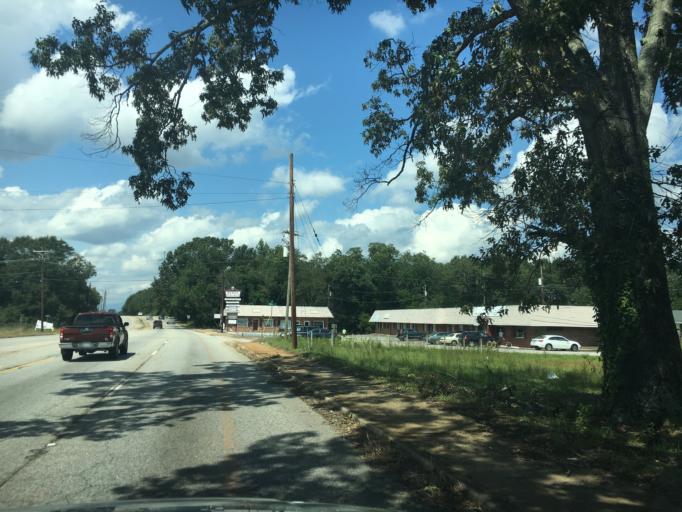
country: US
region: South Carolina
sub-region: Greenville County
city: Berea
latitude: 34.8860
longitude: -82.4601
